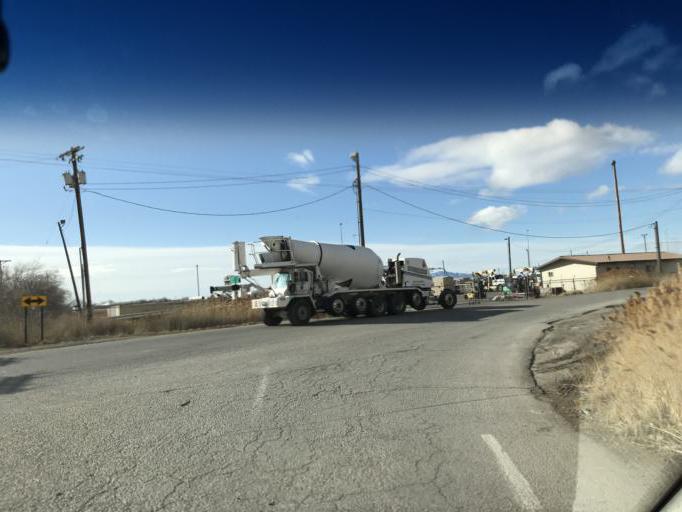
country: US
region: Utah
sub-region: Davis County
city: North Salt Lake
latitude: 40.8057
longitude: -111.9205
